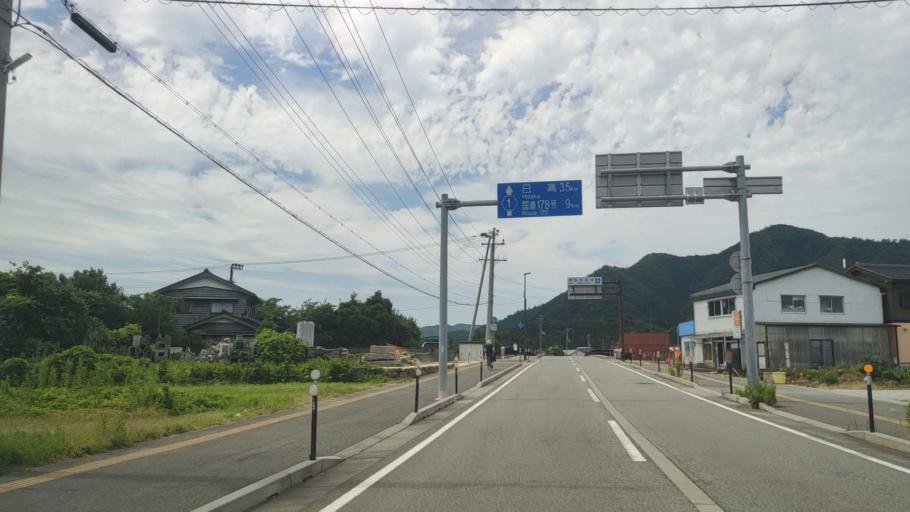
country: JP
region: Hyogo
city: Toyooka
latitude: 35.6550
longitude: 134.7610
